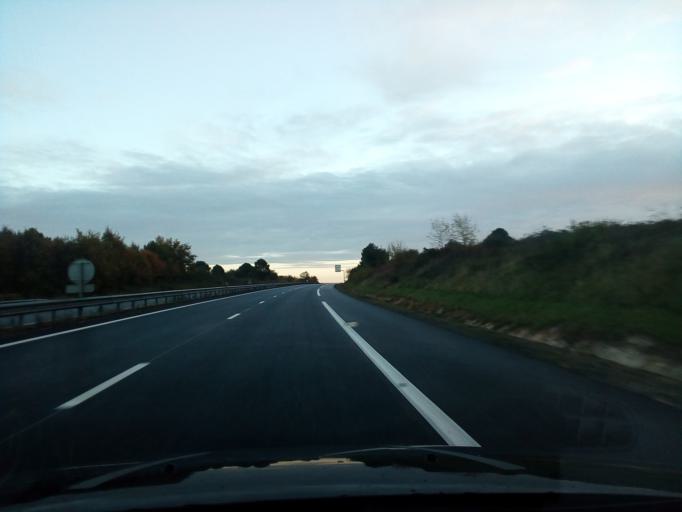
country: FR
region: Poitou-Charentes
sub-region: Departement de la Charente-Maritime
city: Montlieu-la-Garde
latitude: 45.2383
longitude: -0.2752
